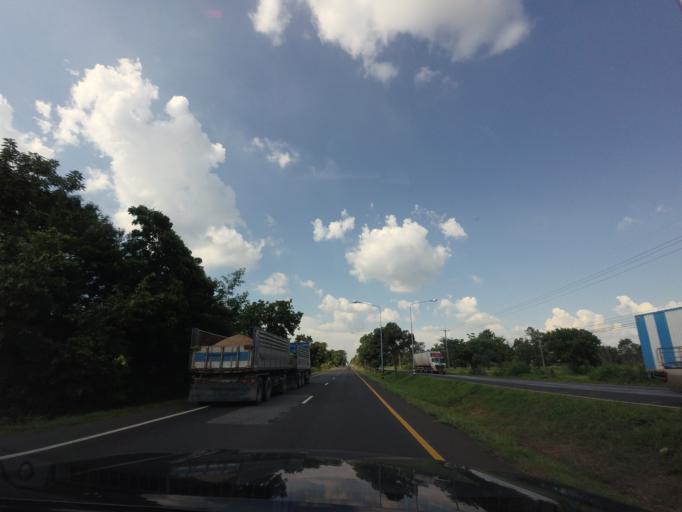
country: TH
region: Nakhon Ratchasima
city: Bua Lai
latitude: 15.7065
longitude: 102.5862
